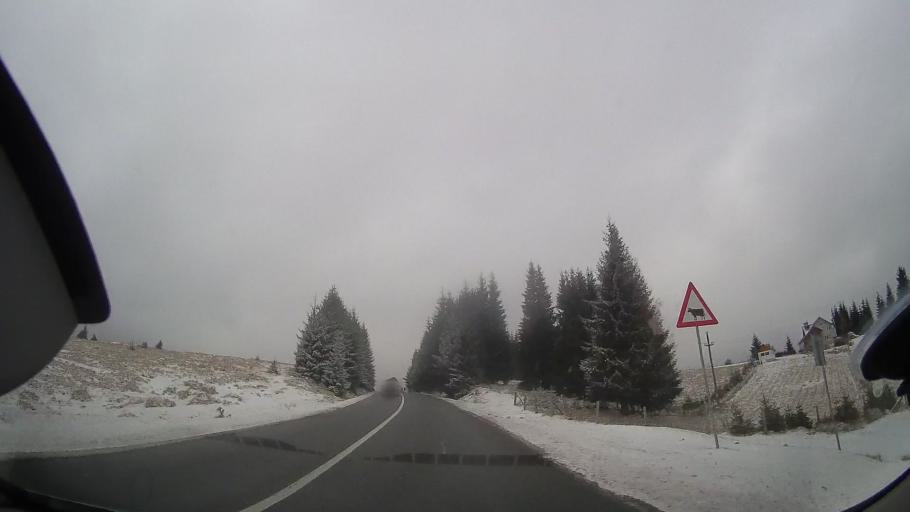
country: RO
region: Cluj
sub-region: Comuna Belis
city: Belis
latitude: 46.6787
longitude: 23.0437
